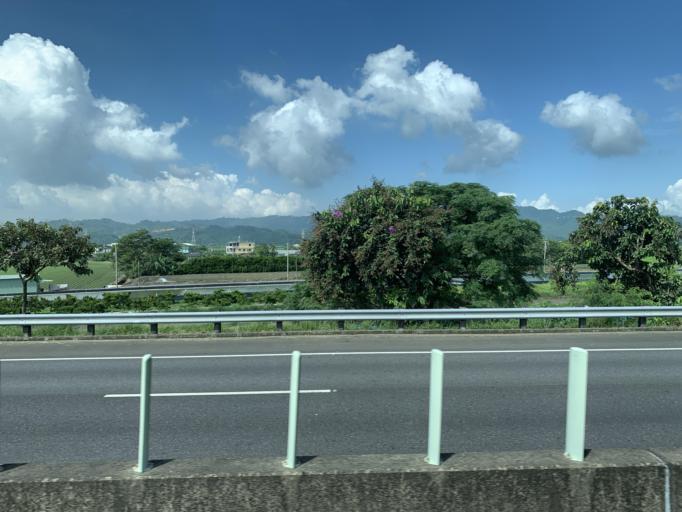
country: TW
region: Taiwan
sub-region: Pingtung
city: Pingtung
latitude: 22.8191
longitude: 120.4870
